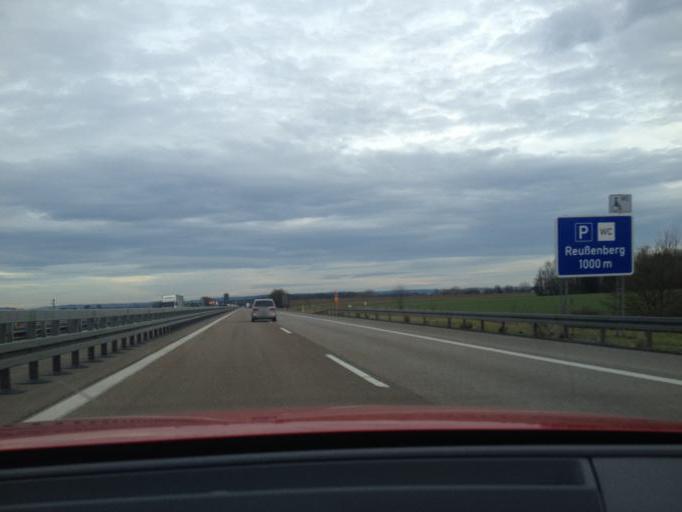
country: DE
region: Baden-Wuerttemberg
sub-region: Regierungsbezirk Stuttgart
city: Kirchberg an der Jagst
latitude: 49.1758
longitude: 9.9765
